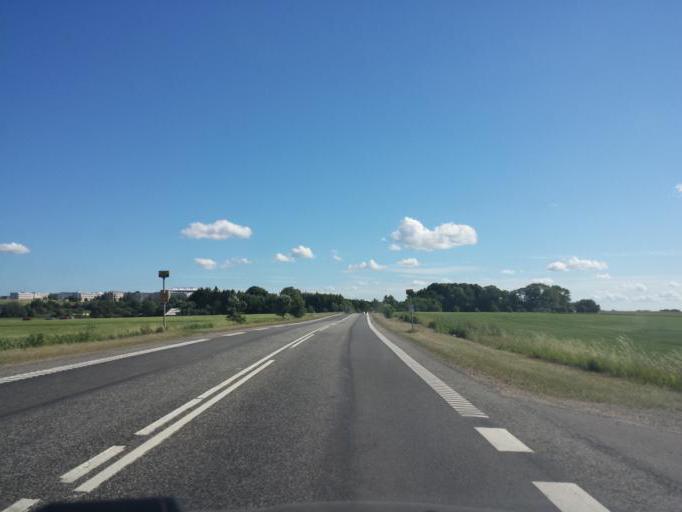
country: DK
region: Capital Region
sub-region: Egedal Kommune
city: Smorumnedre
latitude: 55.7658
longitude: 12.2944
